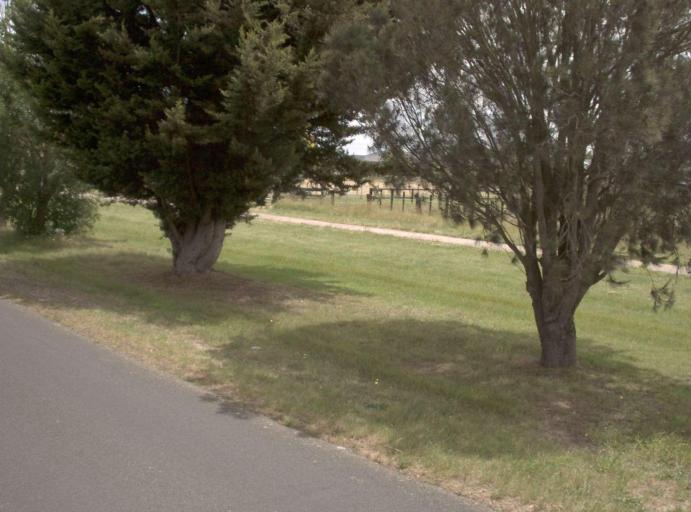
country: AU
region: Victoria
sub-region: Wellington
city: Sale
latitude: -38.1024
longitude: 147.0999
